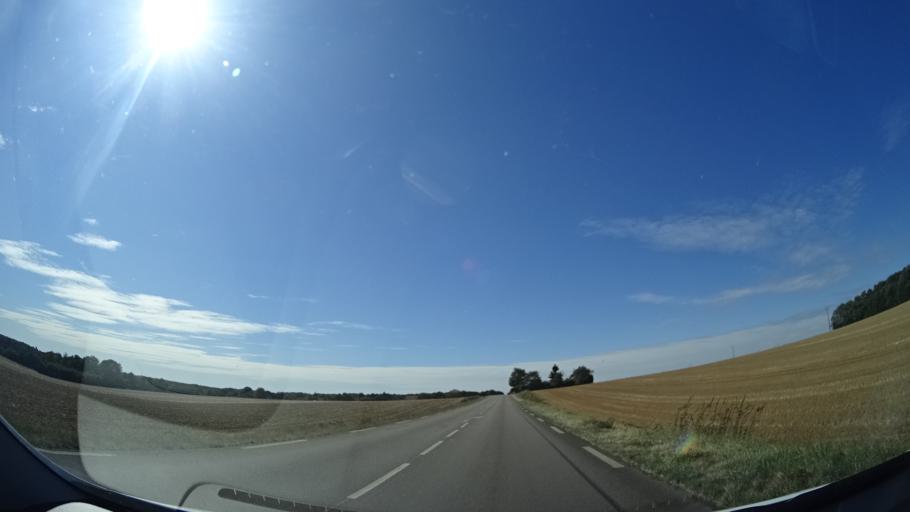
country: FR
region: Bourgogne
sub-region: Departement de l'Yonne
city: Charny
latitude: 47.9312
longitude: 3.1763
